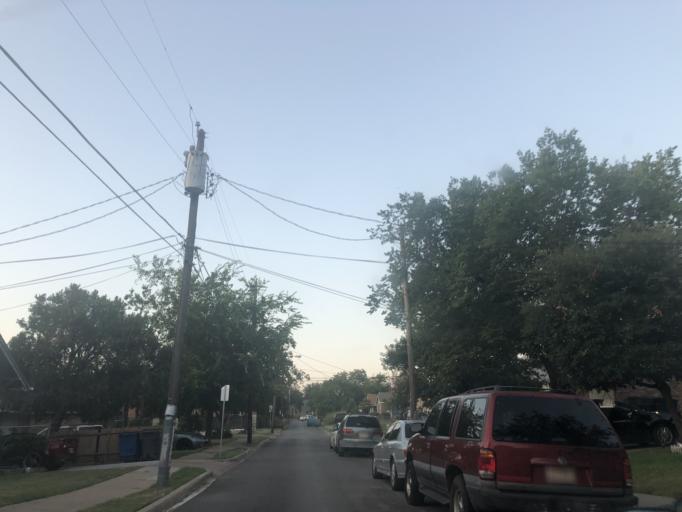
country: US
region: Texas
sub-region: Dallas County
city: Dallas
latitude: 32.7525
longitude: -96.8176
